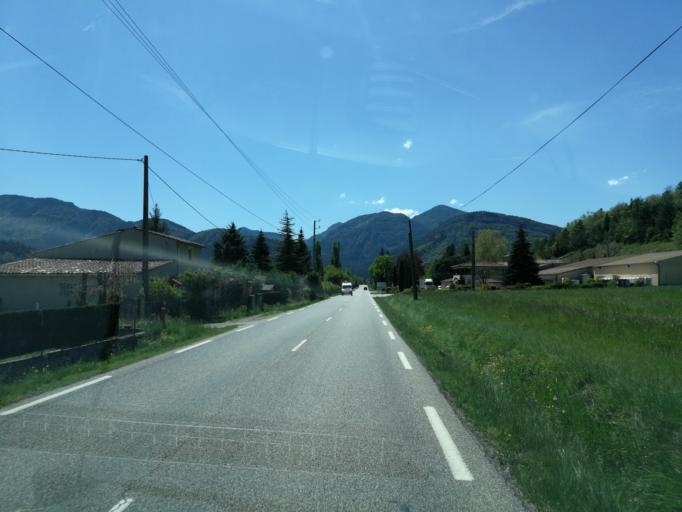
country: FR
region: Rhone-Alpes
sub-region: Departement de la Drome
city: Die
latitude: 44.7160
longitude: 5.2643
